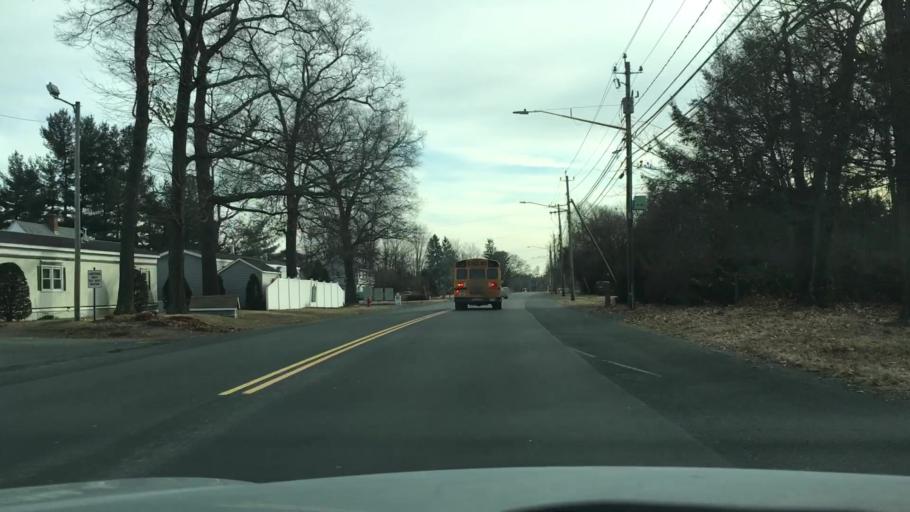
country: US
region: Massachusetts
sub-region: Hampden County
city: Westfield
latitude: 42.0974
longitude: -72.7632
